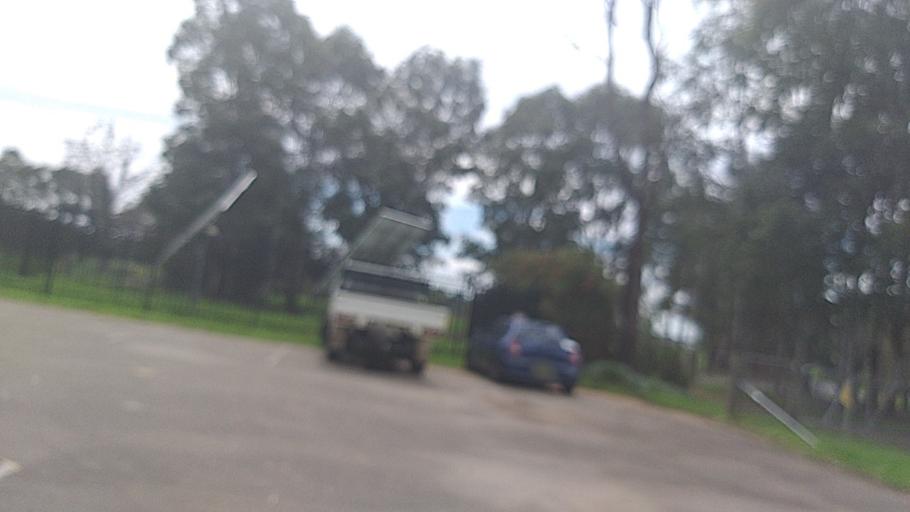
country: AU
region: New South Wales
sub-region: Hawkesbury
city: Richmond
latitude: -33.6116
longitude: 150.7572
